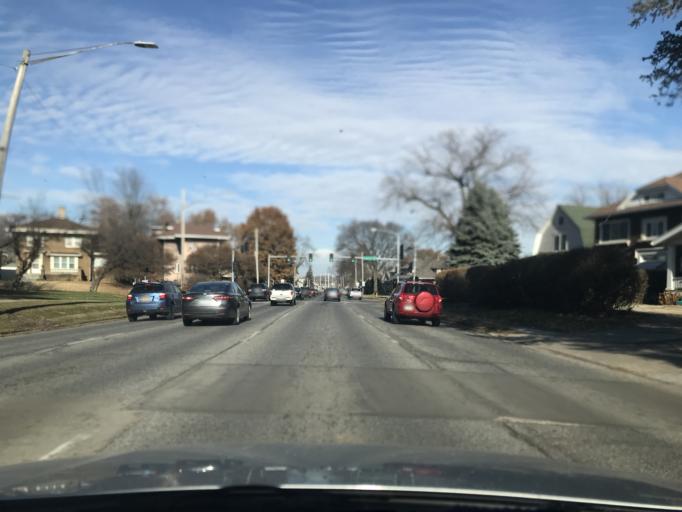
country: US
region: Iowa
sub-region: Scott County
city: Davenport
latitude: 41.5450
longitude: -90.5725
